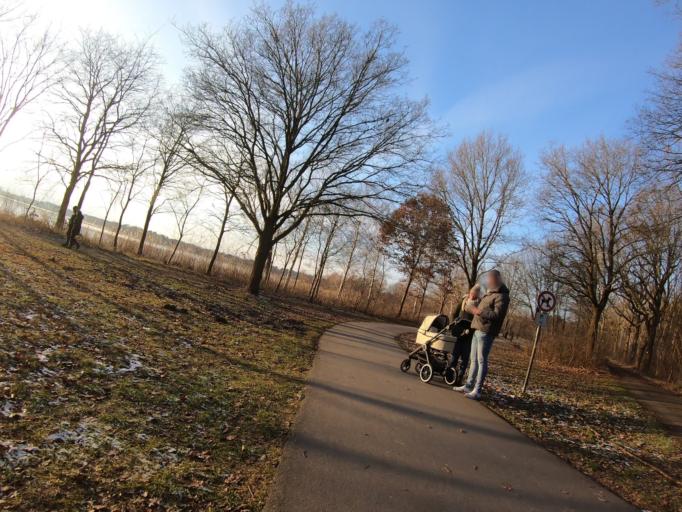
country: DE
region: Lower Saxony
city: Calberlah
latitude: 52.4536
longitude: 10.6297
